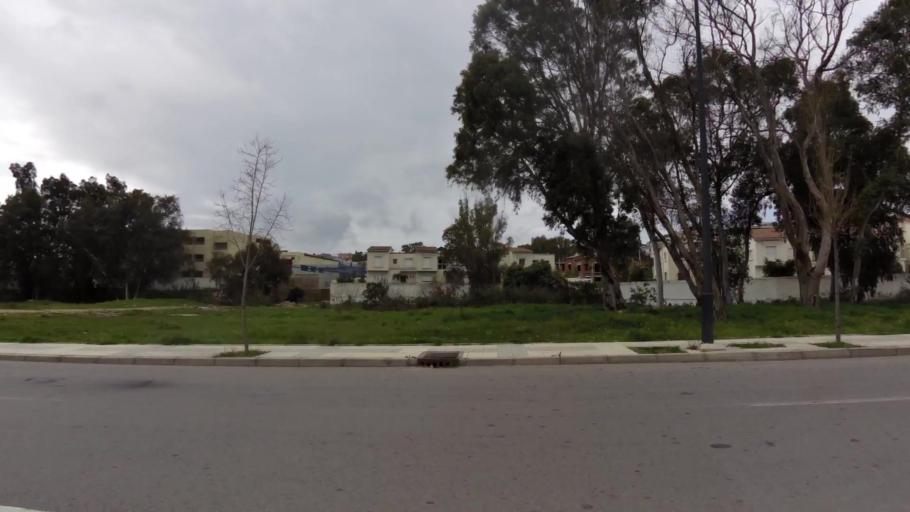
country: MA
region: Tanger-Tetouan
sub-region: Tanger-Assilah
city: Tangier
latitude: 35.7750
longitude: -5.8579
